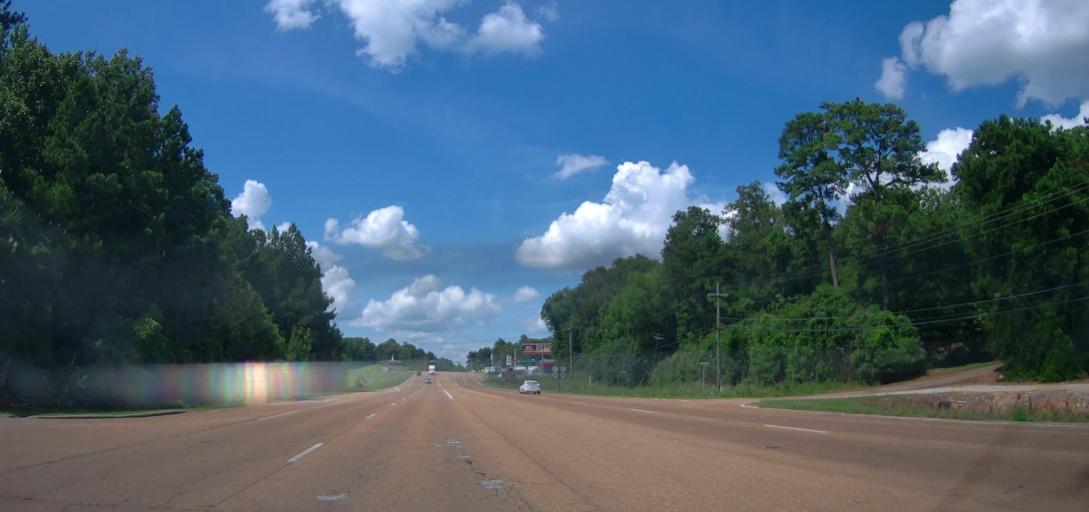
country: US
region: Mississippi
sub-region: Lowndes County
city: Columbus
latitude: 33.5592
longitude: -88.4330
